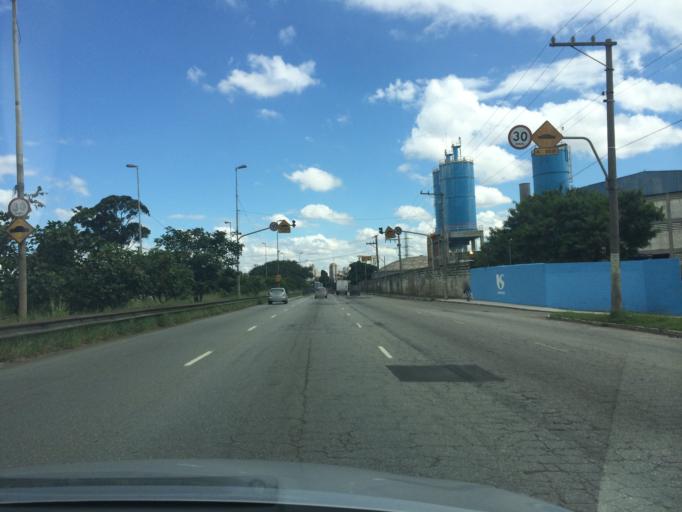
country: BR
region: Sao Paulo
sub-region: Guarulhos
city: Guarulhos
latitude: -23.5128
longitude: -46.5602
